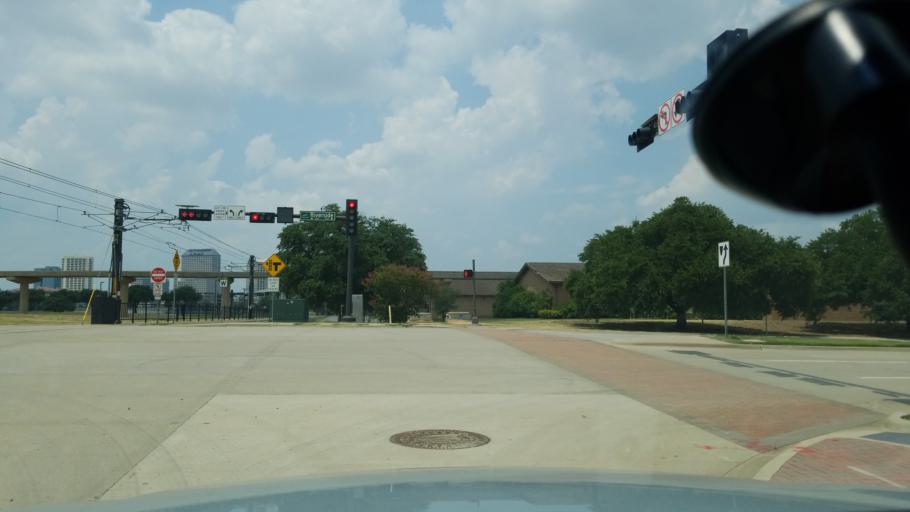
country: US
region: Texas
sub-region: Dallas County
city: Irving
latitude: 32.8597
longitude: -96.9272
